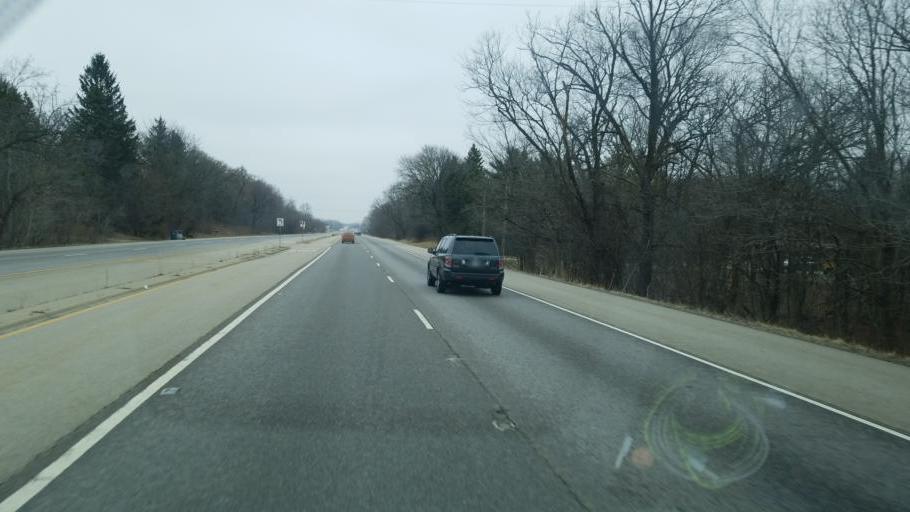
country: US
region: Illinois
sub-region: Lake County
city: Wadsworth
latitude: 42.4555
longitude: -87.9458
